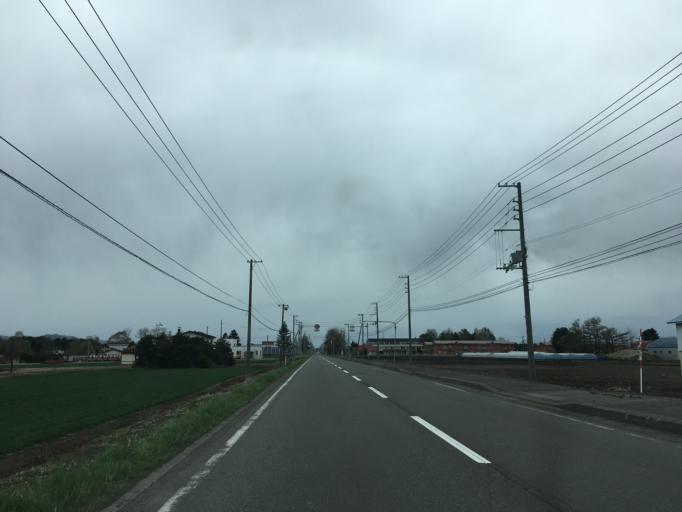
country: JP
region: Hokkaido
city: Chitose
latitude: 42.9375
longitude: 141.8054
